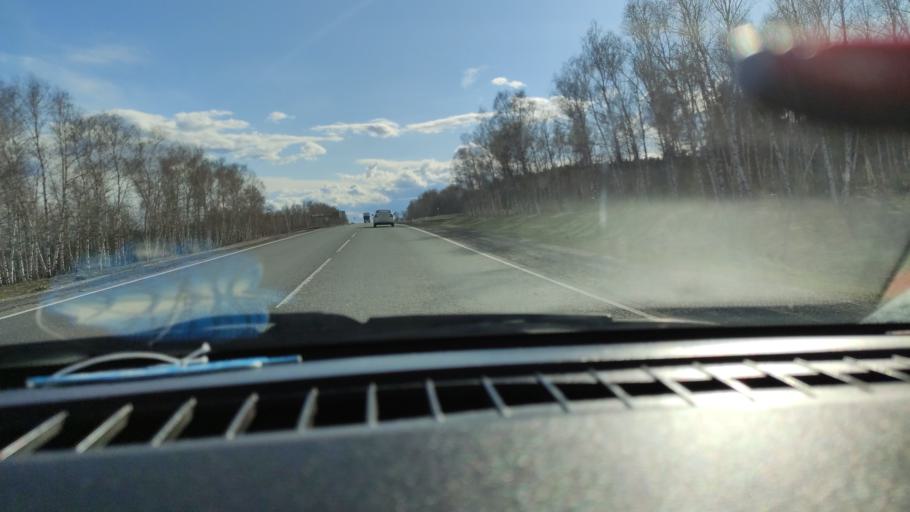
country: RU
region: Saratov
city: Sennoy
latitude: 52.1180
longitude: 46.8410
